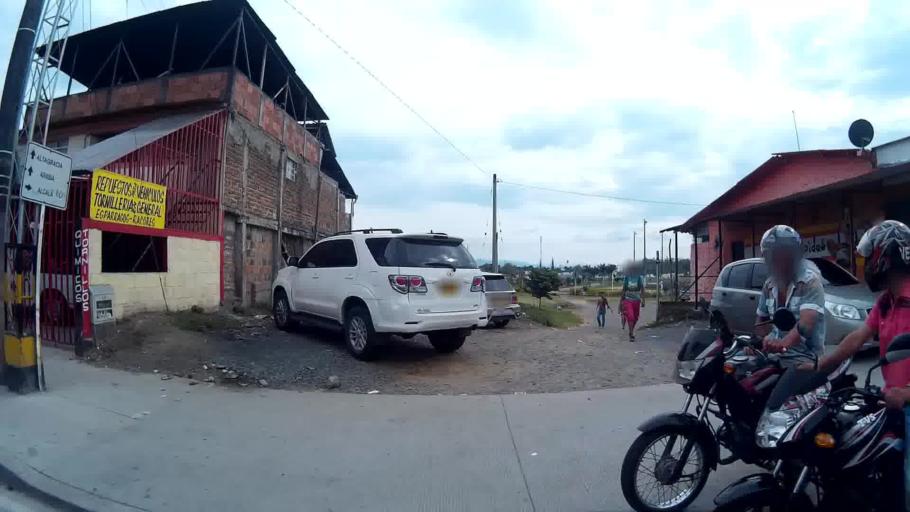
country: CO
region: Risaralda
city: Pereira
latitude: 4.7932
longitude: -75.7376
